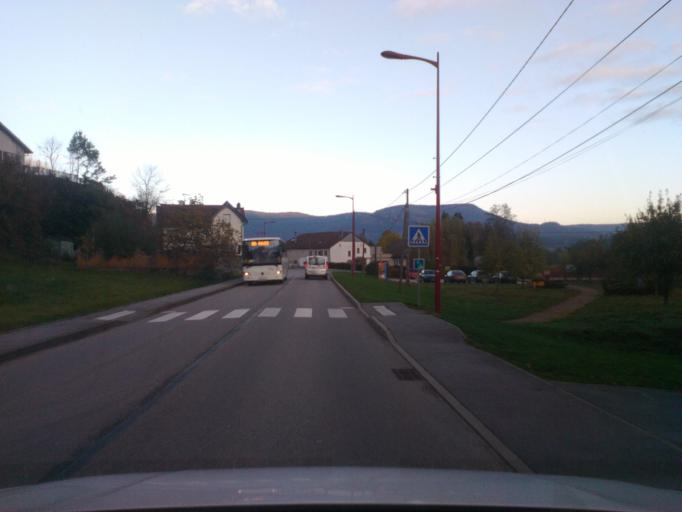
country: FR
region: Lorraine
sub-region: Departement des Vosges
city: Ban-de-Laveline
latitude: 48.2624
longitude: 7.0508
